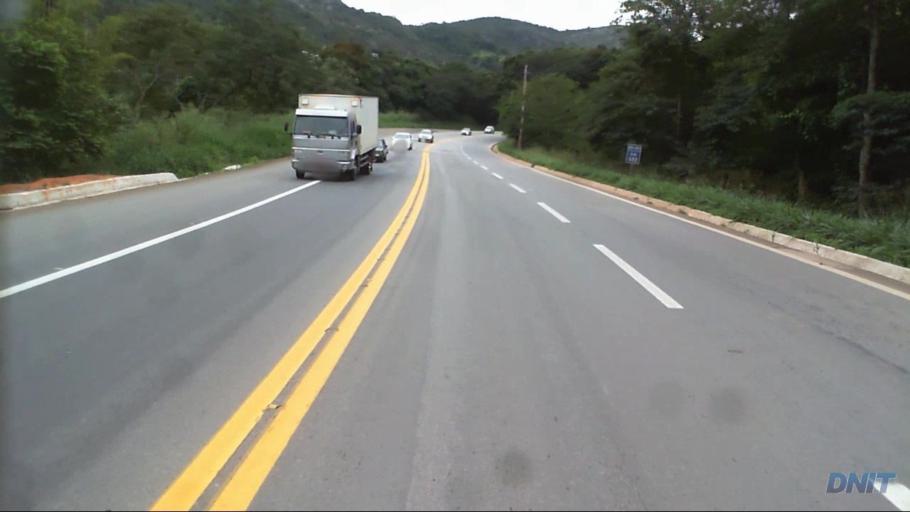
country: BR
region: Minas Gerais
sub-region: Barao De Cocais
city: Barao de Cocais
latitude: -19.7374
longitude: -43.5109
